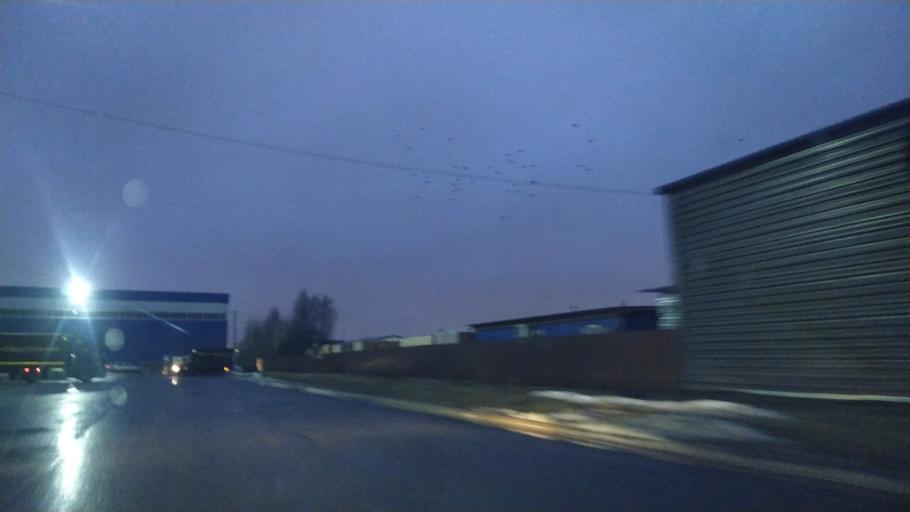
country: RU
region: Leningrad
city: Bugry
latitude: 60.0633
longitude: 30.3809
